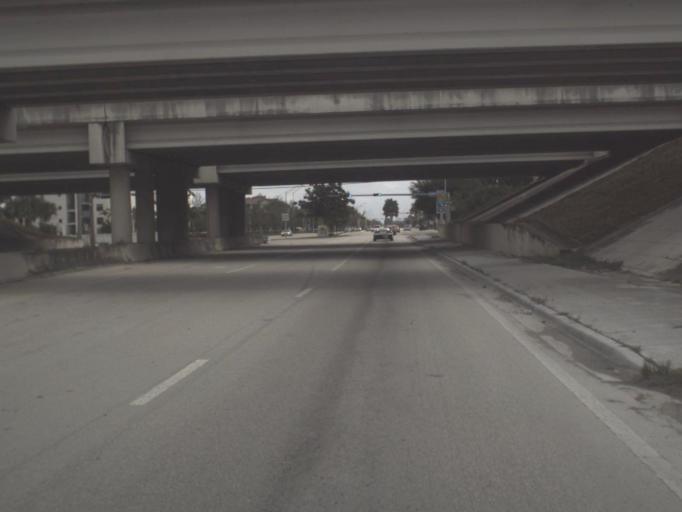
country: US
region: Florida
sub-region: Miami-Dade County
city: Doral
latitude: 25.8116
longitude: -80.3870
